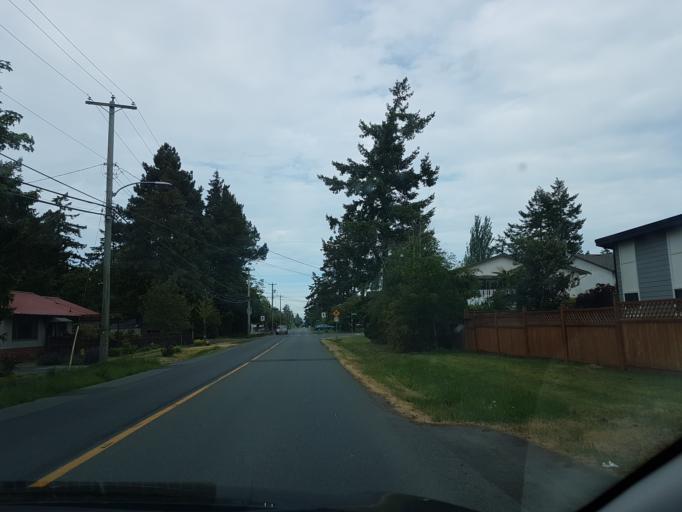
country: CA
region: British Columbia
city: Oak Bay
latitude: 48.4855
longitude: -123.3326
